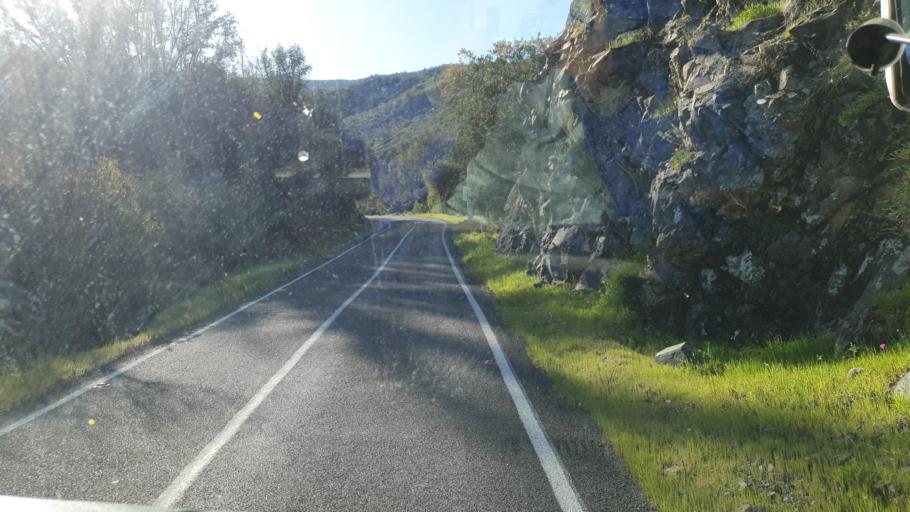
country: CL
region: Valparaiso
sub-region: Provincia de Marga Marga
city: Limache
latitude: -33.1800
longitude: -71.1802
